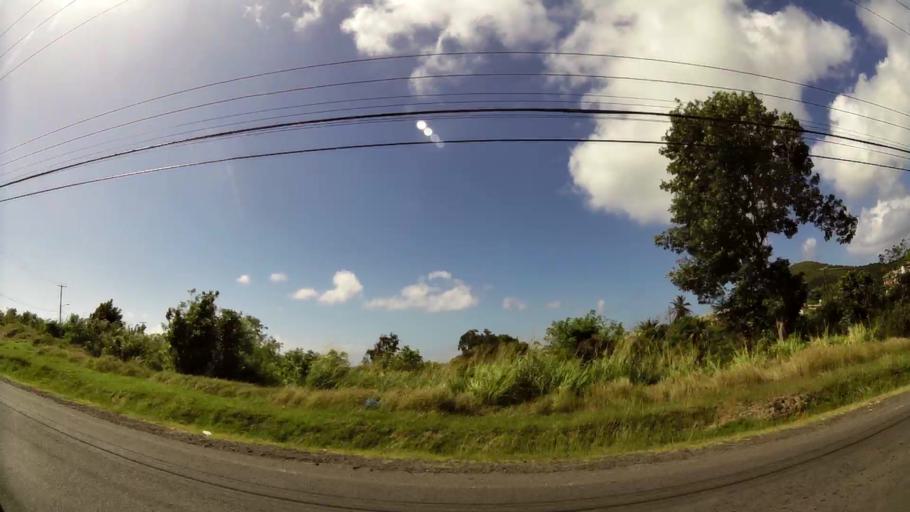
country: LC
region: Laborie Quarter
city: Laborie
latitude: 13.7439
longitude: -60.9790
